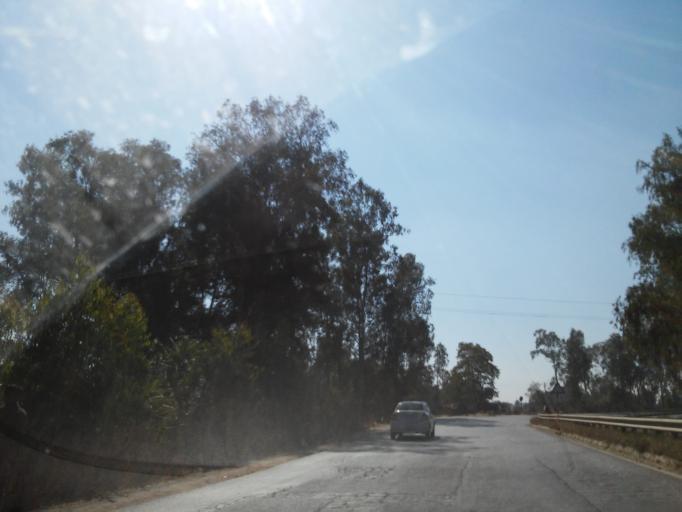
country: IN
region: Rajasthan
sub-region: Dungarpur
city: Dungarpur
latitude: 23.7799
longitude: 73.5171
